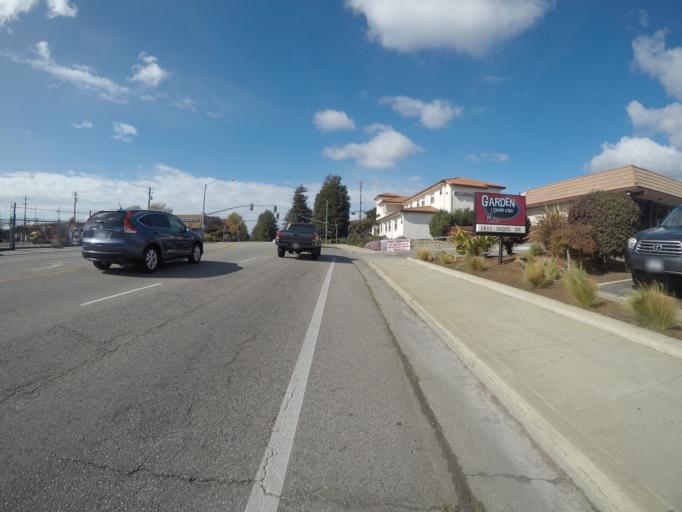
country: US
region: California
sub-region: Santa Cruz County
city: Live Oak
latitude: 36.9890
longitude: -121.9800
